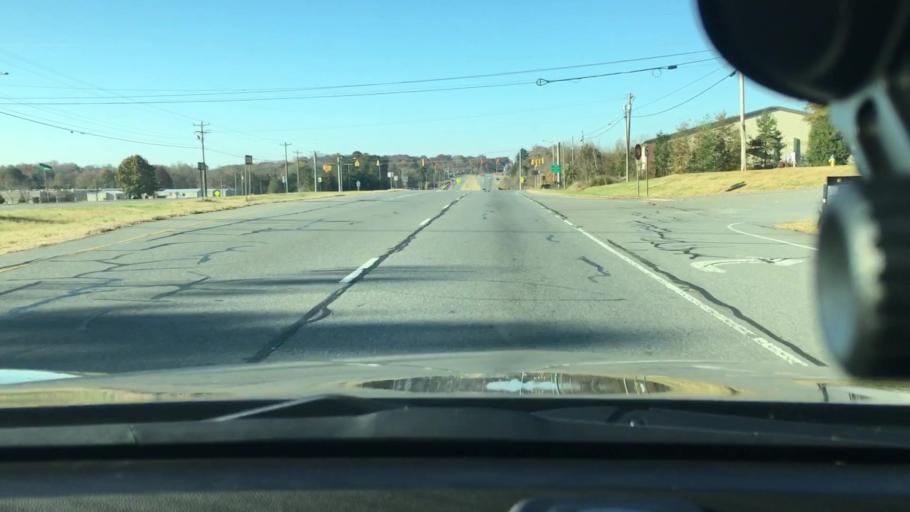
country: US
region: North Carolina
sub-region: Cabarrus County
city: Concord
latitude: 35.3654
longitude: -80.5825
